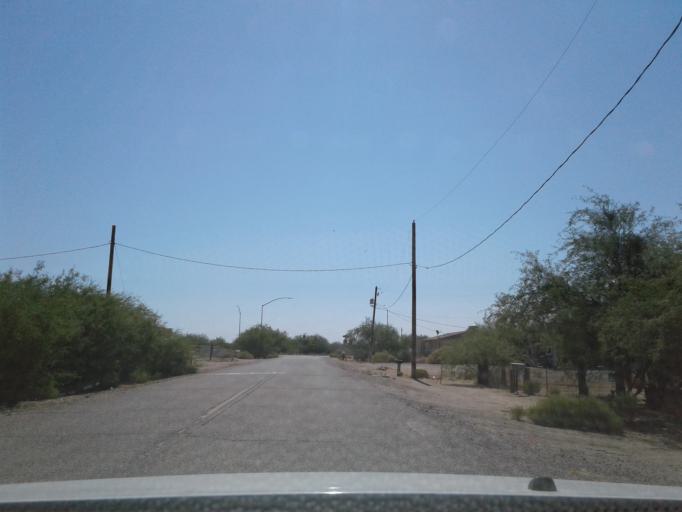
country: US
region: Arizona
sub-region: Maricopa County
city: Laveen
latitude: 33.2881
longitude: -112.1706
